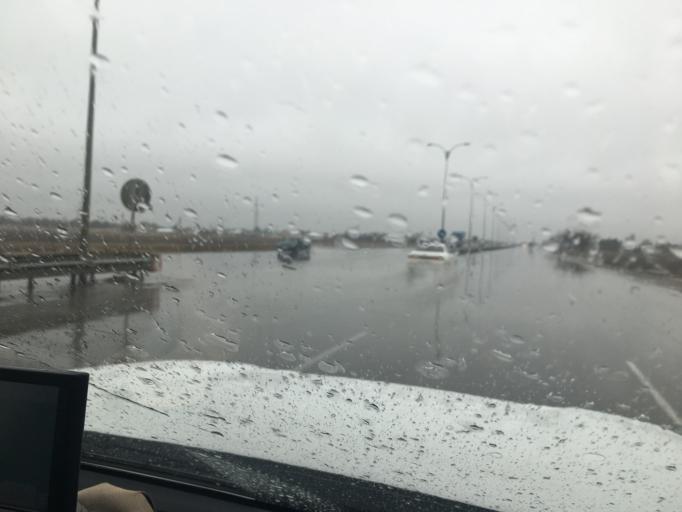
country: TM
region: Mary
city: Mary
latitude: 37.5554
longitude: 61.8565
